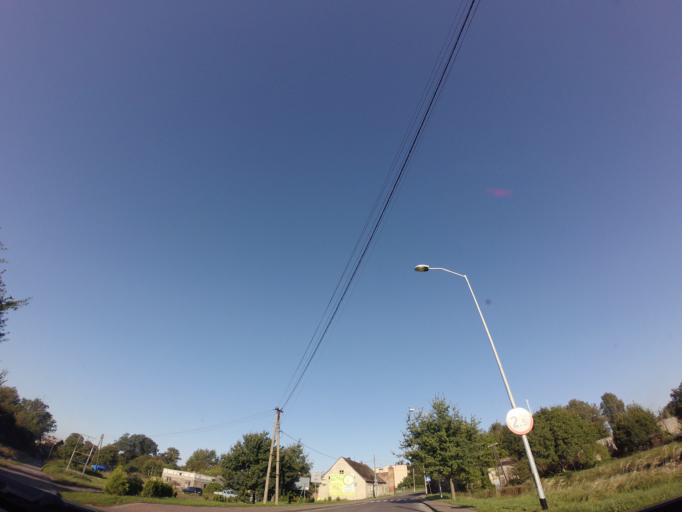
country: PL
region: West Pomeranian Voivodeship
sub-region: Powiat goleniowski
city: Maszewo
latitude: 53.4940
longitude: 15.0651
